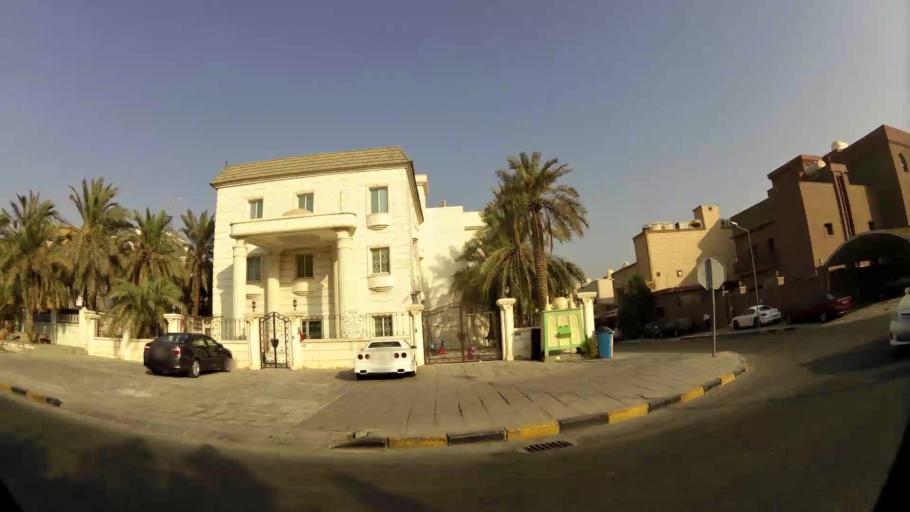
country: KW
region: Muhafazat Hawalli
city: Ar Rumaythiyah
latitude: 29.3220
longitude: 48.0772
